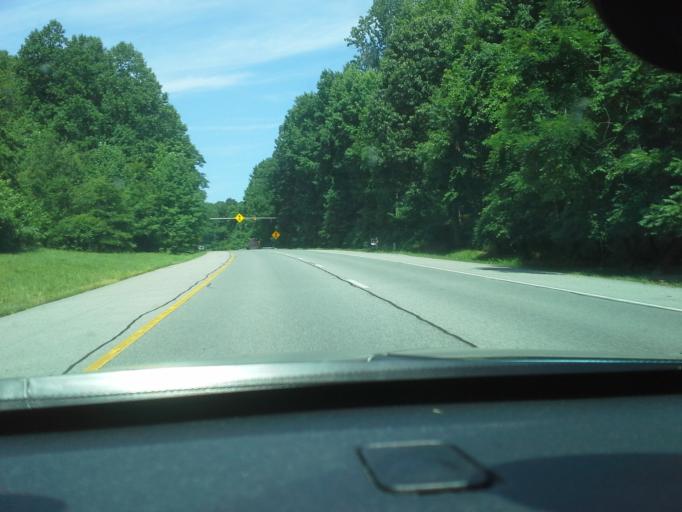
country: US
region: Maryland
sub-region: Calvert County
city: Owings
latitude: 38.7036
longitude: -76.5694
